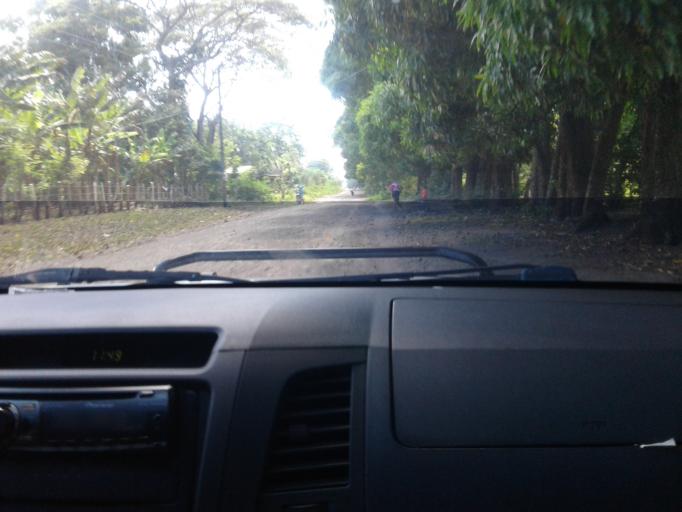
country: NI
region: Rivas
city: Altagracia
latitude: 11.4538
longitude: -85.5623
